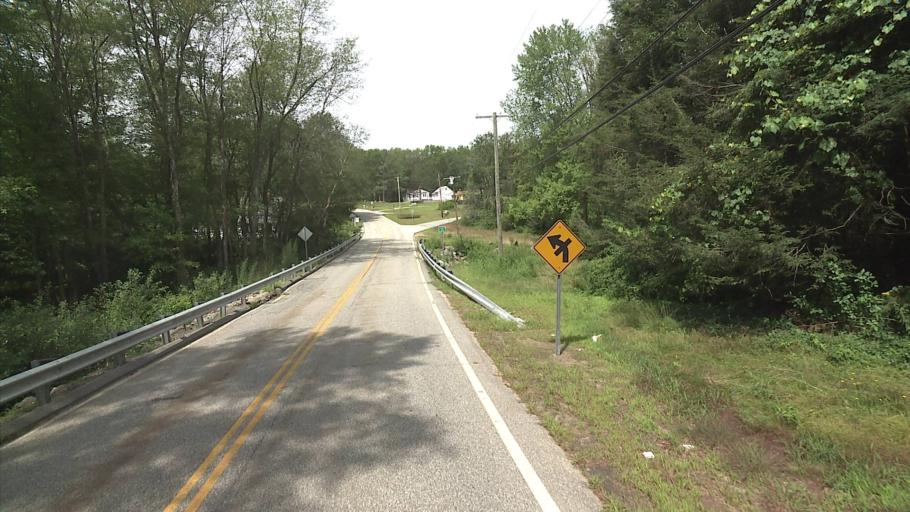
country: US
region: Connecticut
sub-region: Windham County
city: North Grosvenor Dale
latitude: 41.9707
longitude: -71.8854
